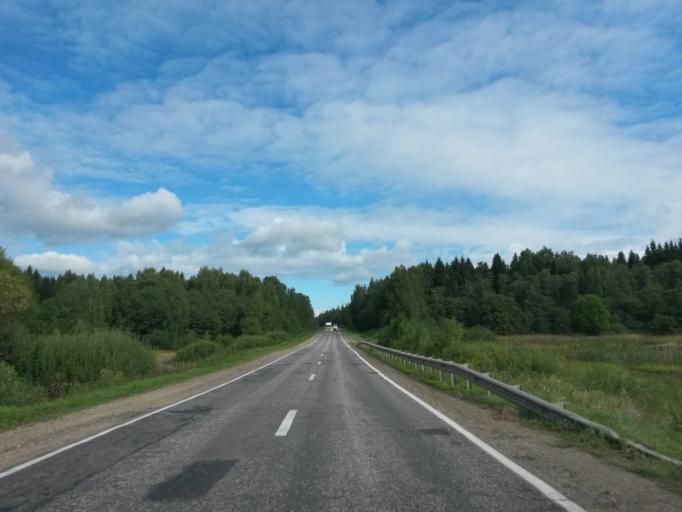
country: RU
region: Jaroslavl
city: Krasnyye Tkachi
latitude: 57.4660
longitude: 39.9086
